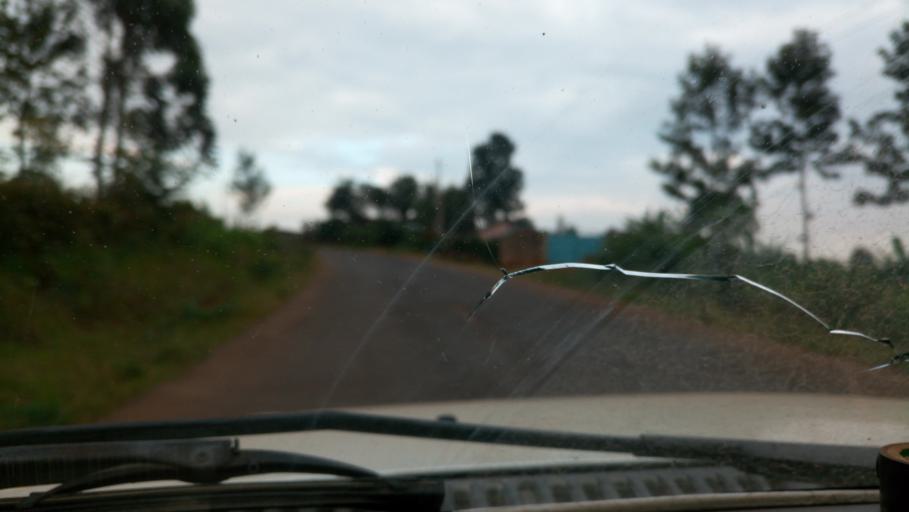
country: KE
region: Murang'a District
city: Kangema
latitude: -0.6542
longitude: 36.9209
